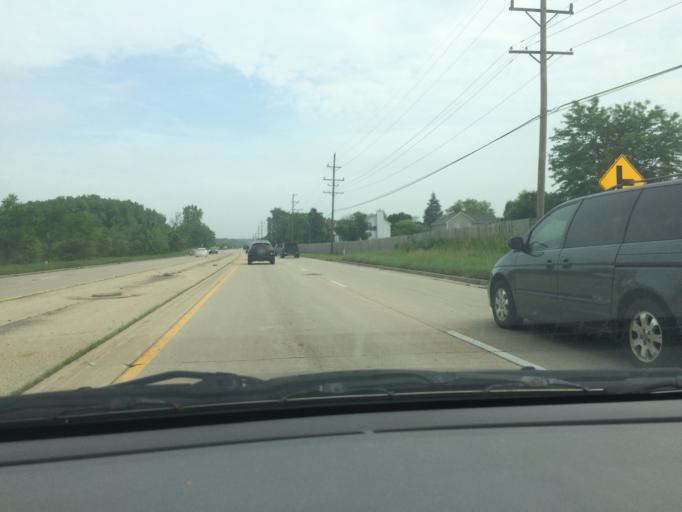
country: US
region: Illinois
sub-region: Cook County
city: Bartlett
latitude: 41.9662
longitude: -88.2064
